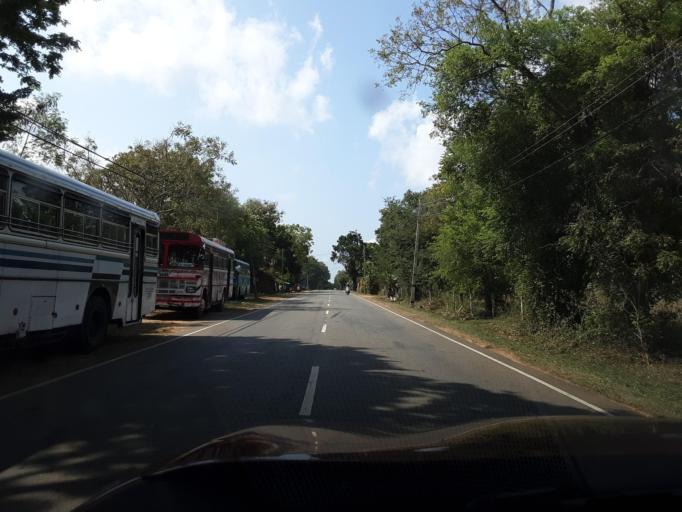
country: LK
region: Southern
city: Tangalla
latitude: 6.2589
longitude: 81.2266
